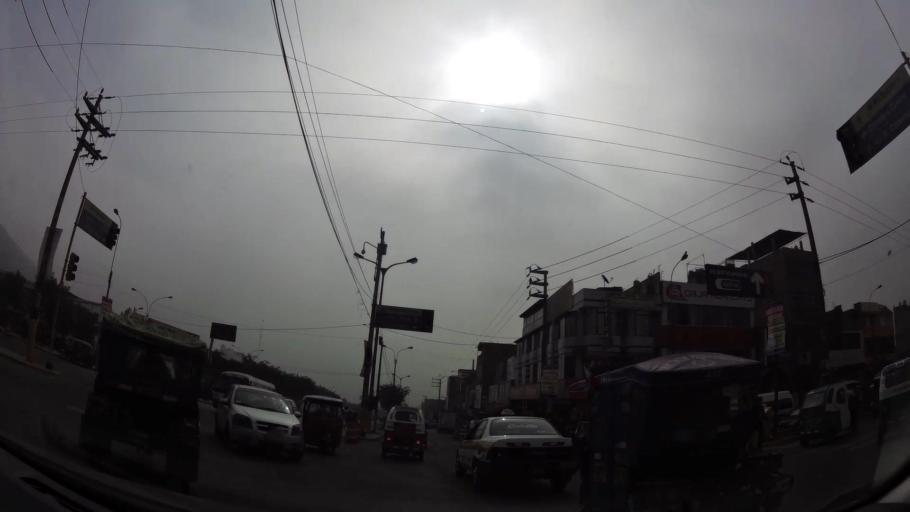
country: PE
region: Lima
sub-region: Lima
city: Chaclacayo
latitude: -12.0135
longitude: -76.8249
